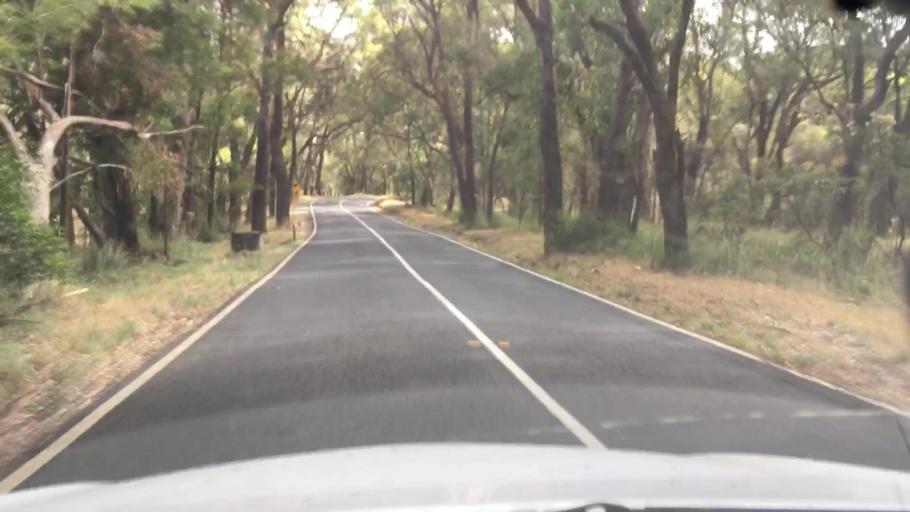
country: AU
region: Victoria
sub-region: Yarra Ranges
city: Macclesfield
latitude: -37.8546
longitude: 145.4833
